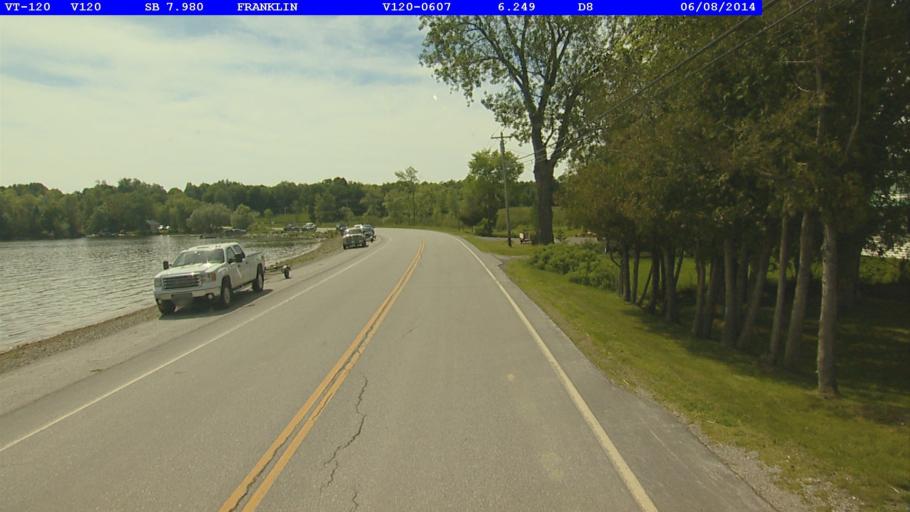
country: US
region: Vermont
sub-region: Franklin County
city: Enosburg Falls
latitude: 44.9906
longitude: -72.8697
